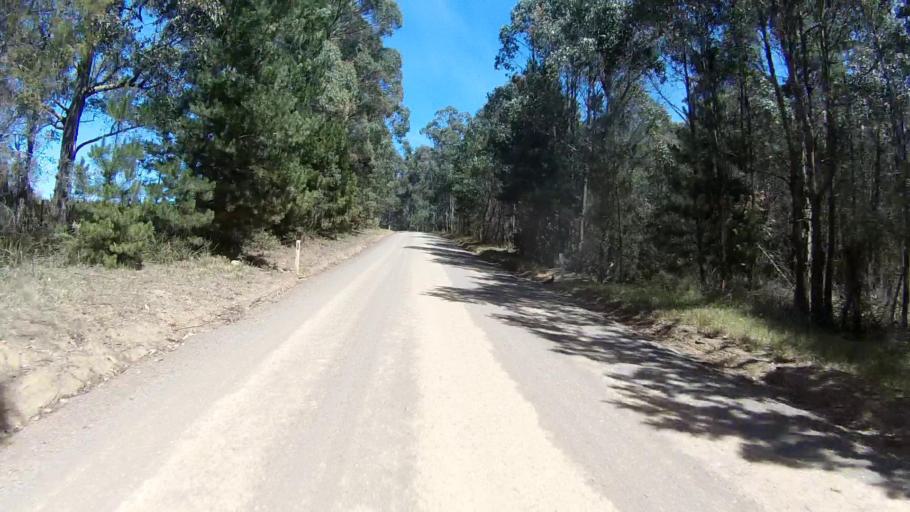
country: AU
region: Tasmania
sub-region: Sorell
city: Sorell
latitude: -42.7527
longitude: 147.6934
